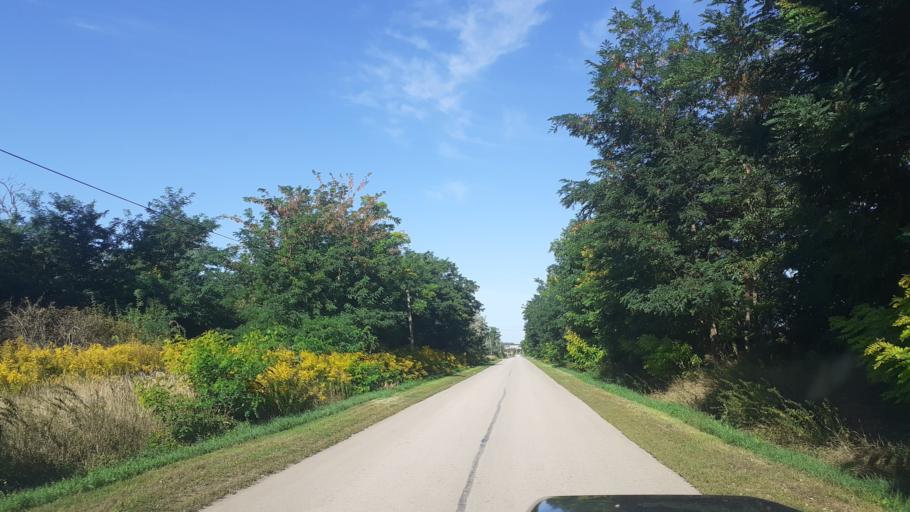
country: HU
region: Fejer
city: Pusztaszabolcs
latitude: 47.1917
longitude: 18.7735
